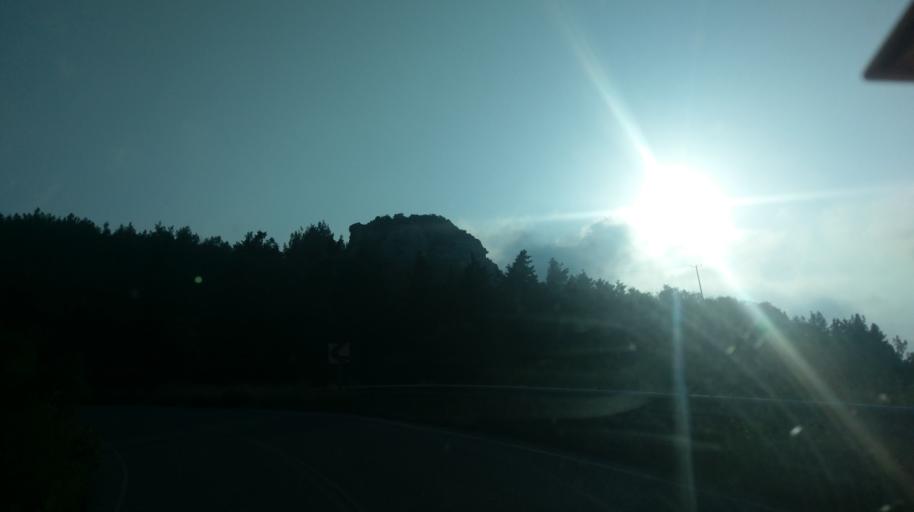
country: CY
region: Ammochostos
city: Trikomo
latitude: 35.3956
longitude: 33.8979
